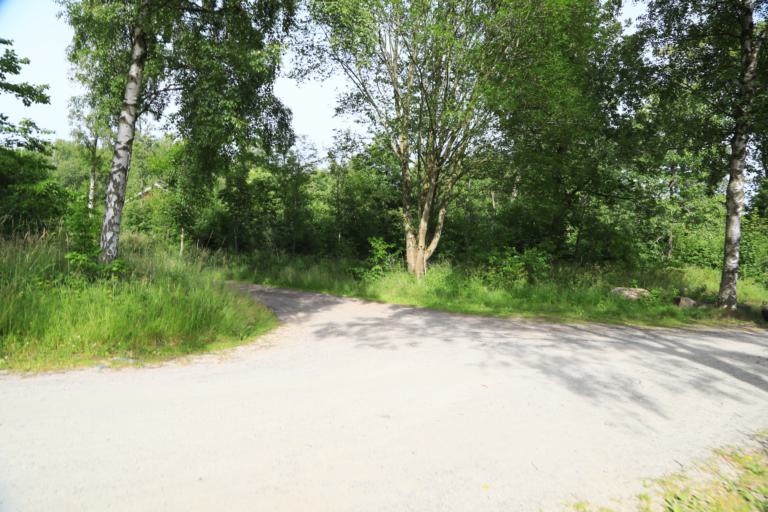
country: SE
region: Halland
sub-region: Varbergs Kommun
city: Traslovslage
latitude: 57.0943
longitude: 12.2809
